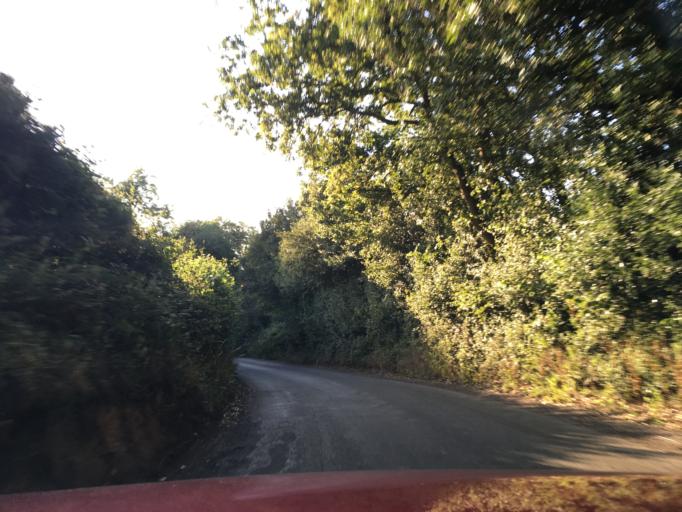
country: GB
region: England
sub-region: West Berkshire
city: Thatcham
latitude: 51.4268
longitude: -1.1846
